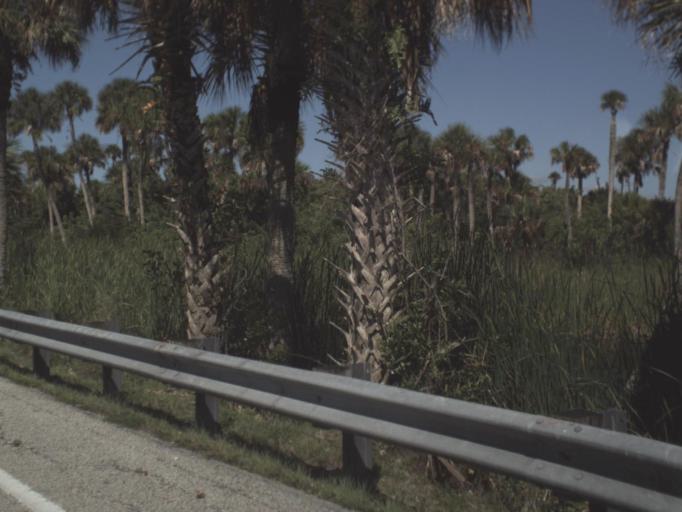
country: US
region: Florida
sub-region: Collier County
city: Marco
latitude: 25.9301
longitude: -81.4379
